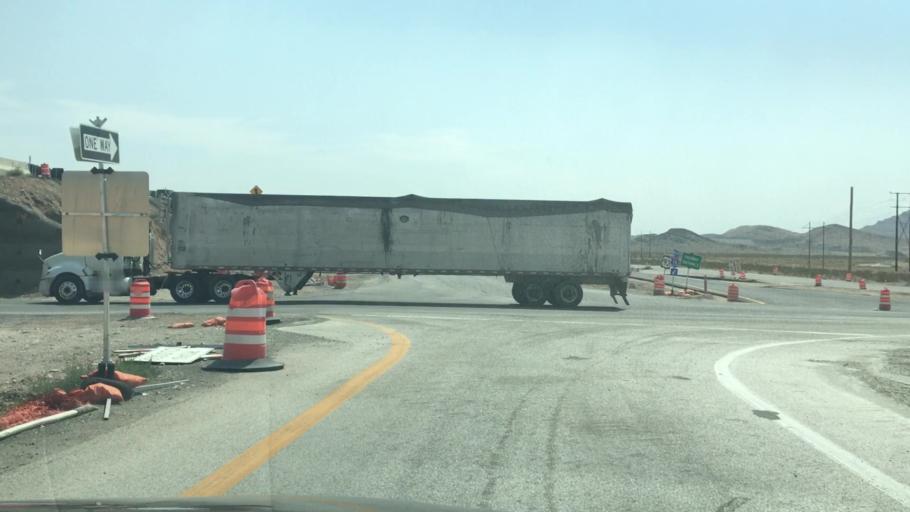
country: US
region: Nevada
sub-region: Clark County
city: Nellis Air Force Base
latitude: 36.3813
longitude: -114.8920
